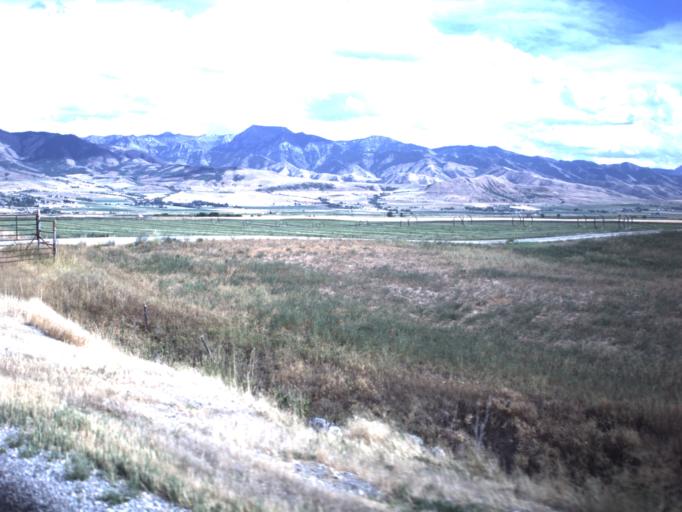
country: US
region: Utah
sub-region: Cache County
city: Lewiston
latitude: 41.9249
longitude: -111.8767
